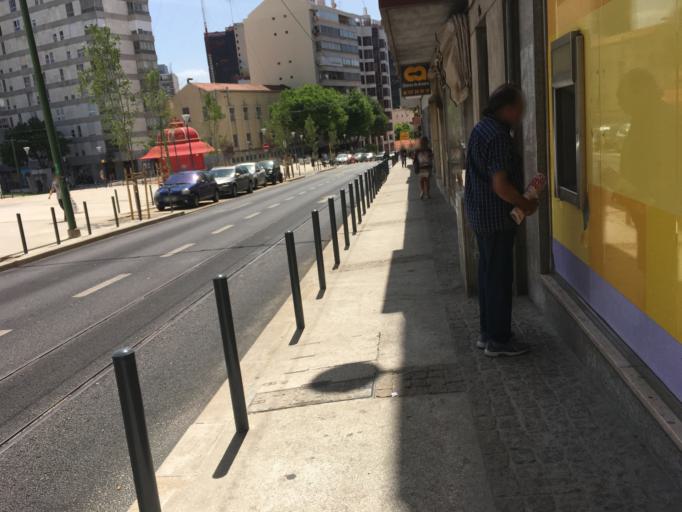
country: PT
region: Lisbon
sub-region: Lisbon
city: Lisbon
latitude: 38.7273
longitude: -9.1623
